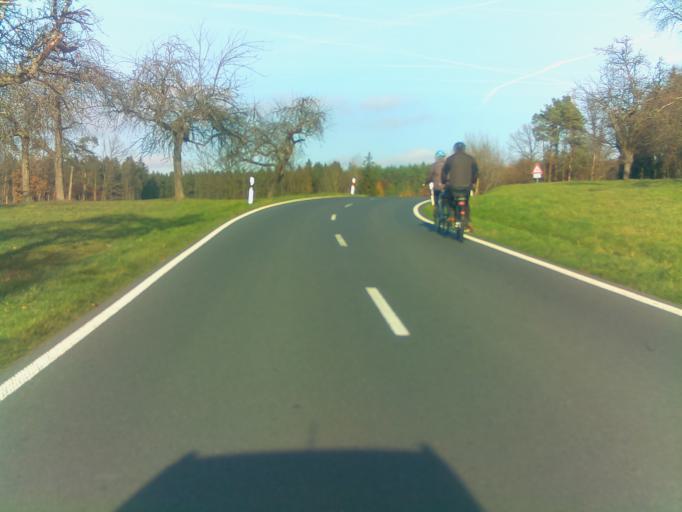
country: DE
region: Bavaria
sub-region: Regierungsbezirk Unterfranken
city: Neunkirchen
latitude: 49.7127
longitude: 9.4123
